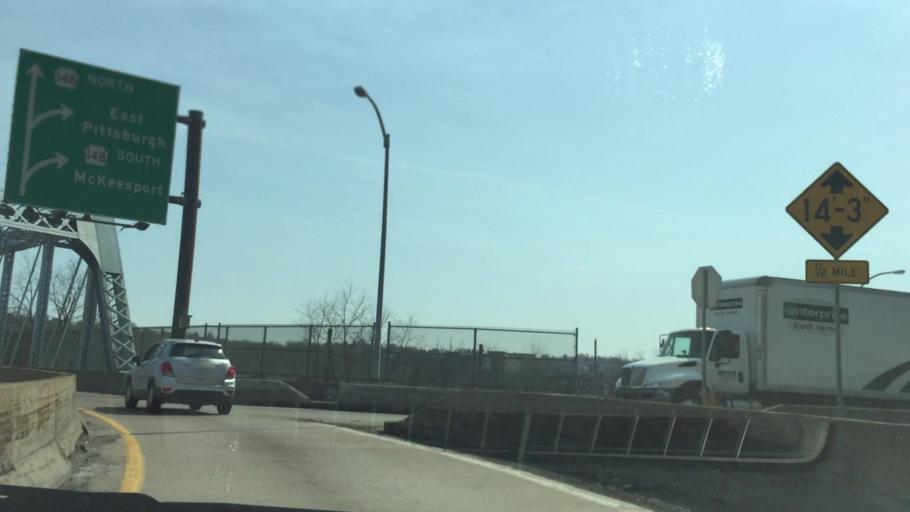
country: US
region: Pennsylvania
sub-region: Allegheny County
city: West Mifflin
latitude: 40.3605
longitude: -79.8454
